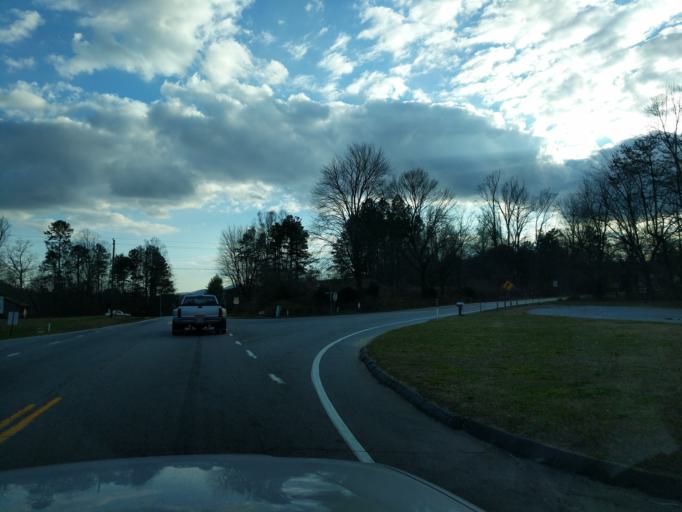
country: US
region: North Carolina
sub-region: McDowell County
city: West Marion
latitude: 35.6154
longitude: -81.9857
